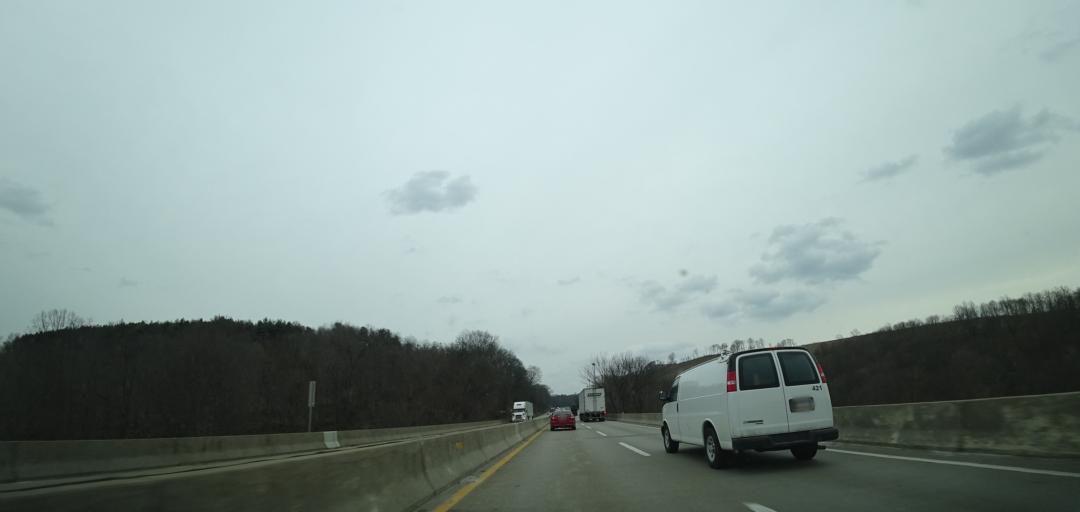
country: US
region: Pennsylvania
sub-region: Beaver County
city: West Mayfield
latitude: 40.8110
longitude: -80.3174
